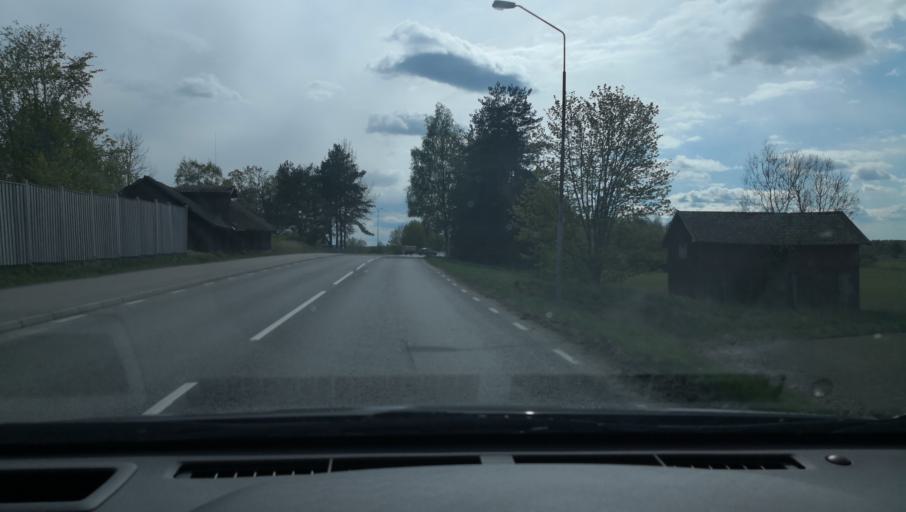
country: SE
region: OErebro
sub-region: Hallsbergs Kommun
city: Hallsberg
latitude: 59.0730
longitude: 15.1379
